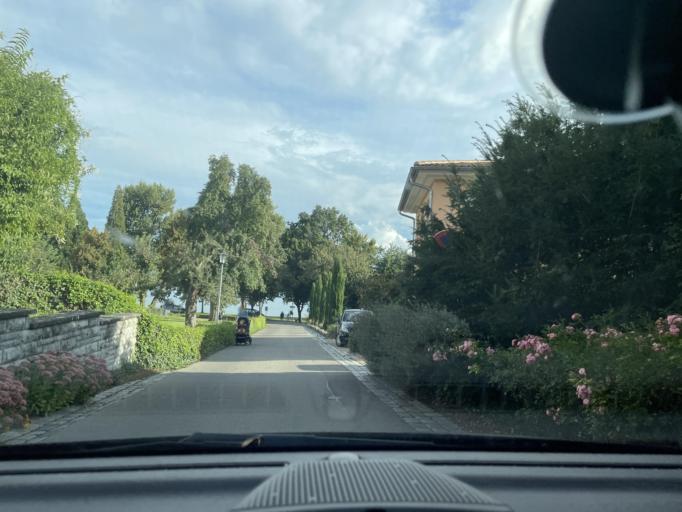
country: DE
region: Baden-Wuerttemberg
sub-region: Tuebingen Region
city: Immenstaad am Bodensee
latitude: 47.6628
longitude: 9.3583
